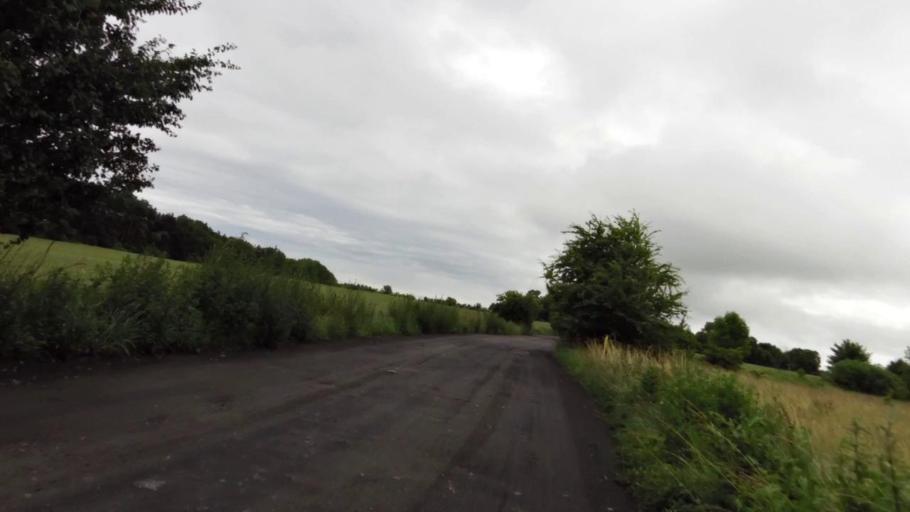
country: PL
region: West Pomeranian Voivodeship
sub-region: Powiat koszalinski
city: Mielno
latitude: 54.2456
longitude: 15.9249
